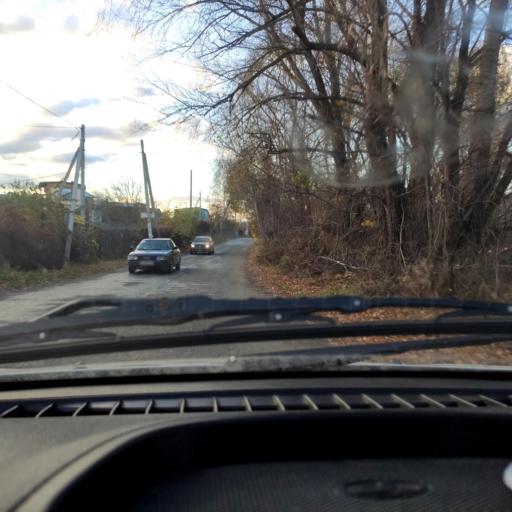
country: RU
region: Samara
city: Povolzhskiy
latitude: 53.4647
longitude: 49.6693
